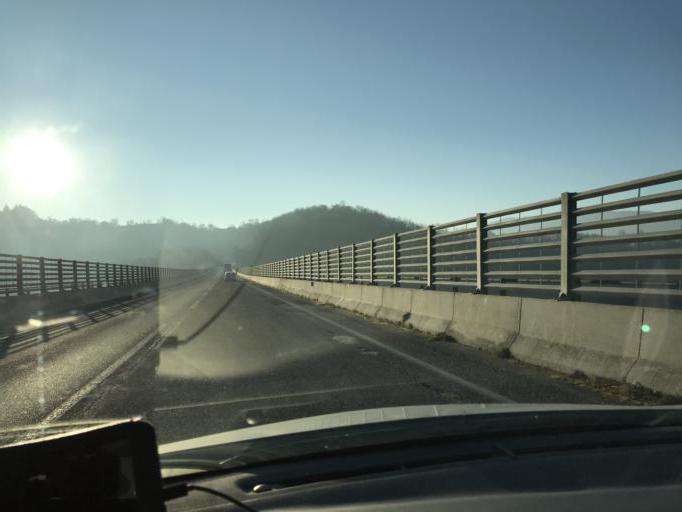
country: IT
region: Latium
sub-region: Provincia di Rieti
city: Pescorocchiano
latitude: 42.2445
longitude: 13.1689
